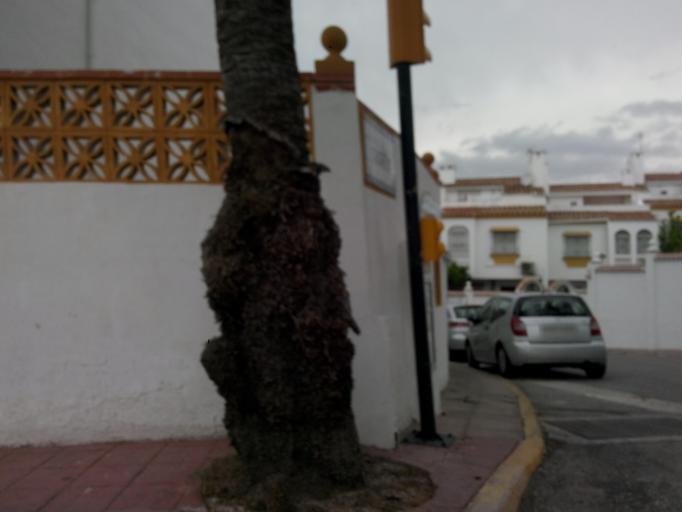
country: ES
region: Andalusia
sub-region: Provincia de Malaga
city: Benalmadena
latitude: 36.5943
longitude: -4.5361
